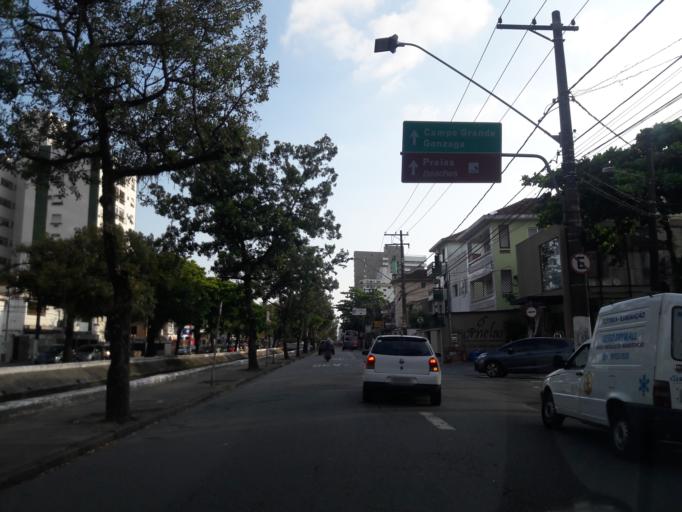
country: BR
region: Sao Paulo
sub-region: Santos
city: Santos
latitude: -23.9520
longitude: -46.3371
